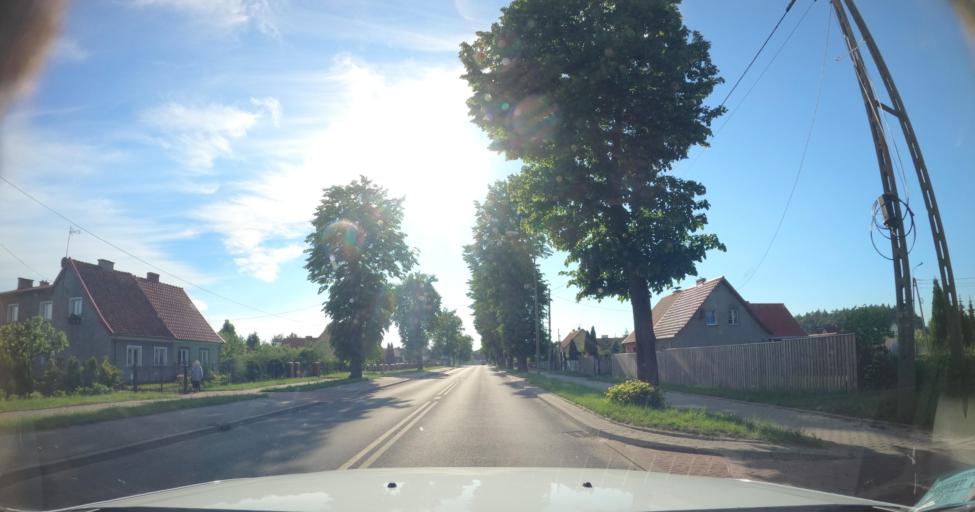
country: PL
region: Warmian-Masurian Voivodeship
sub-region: Powiat elblaski
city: Paslek
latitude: 54.0728
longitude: 19.6451
